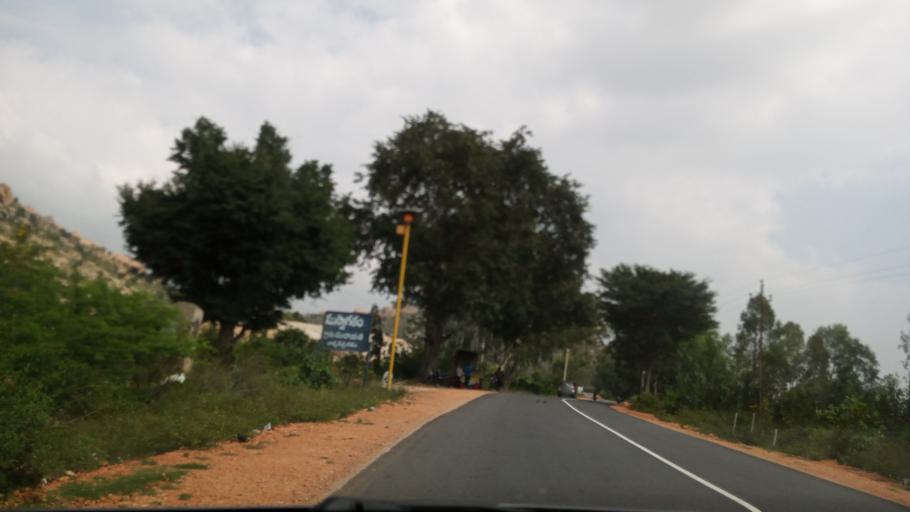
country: IN
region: Andhra Pradesh
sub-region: Chittoor
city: Madanapalle
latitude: 13.6357
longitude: 78.6098
